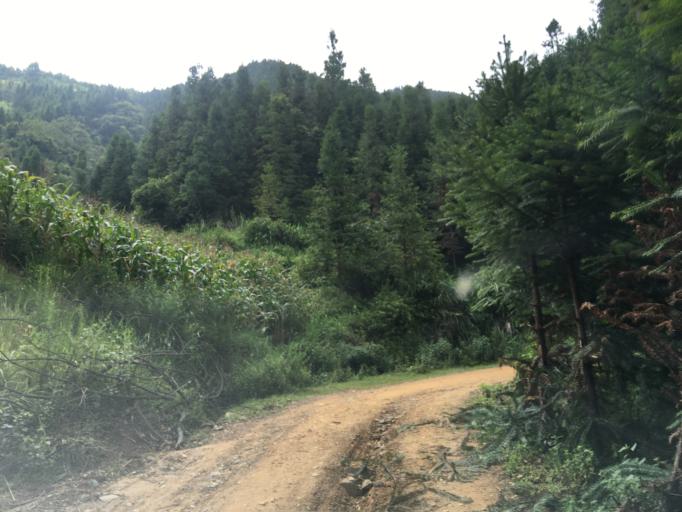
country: CN
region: Guangxi Zhuangzu Zizhiqu
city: Xinzhou
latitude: 24.8796
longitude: 105.8453
